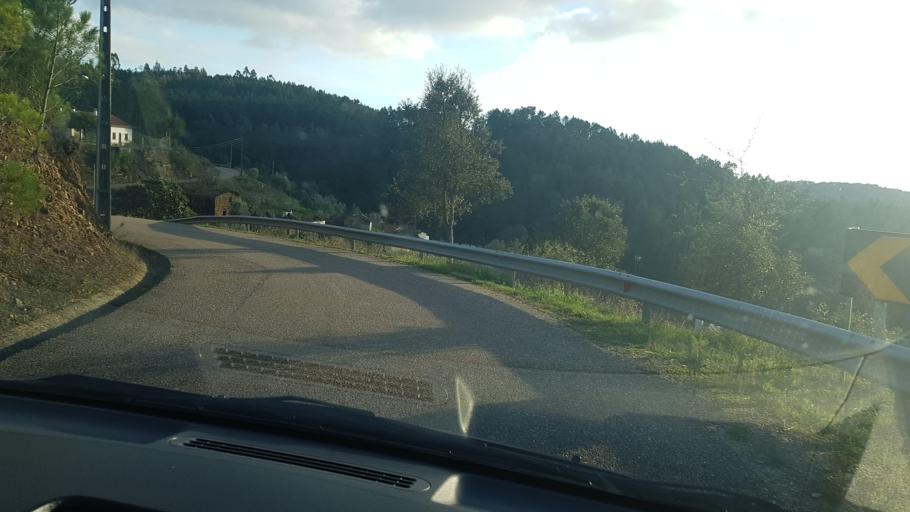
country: PT
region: Castelo Branco
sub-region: Vila de Rei
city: Vila de Rei
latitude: 39.6008
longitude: -8.1213
